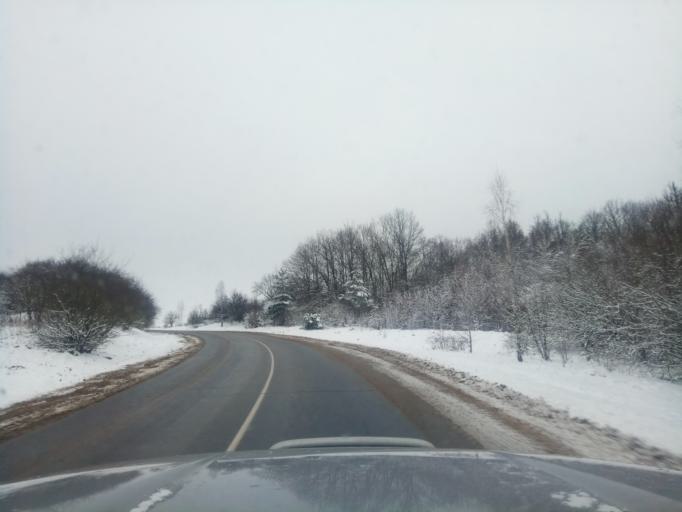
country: BY
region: Minsk
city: Kapyl'
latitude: 53.1545
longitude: 27.1184
